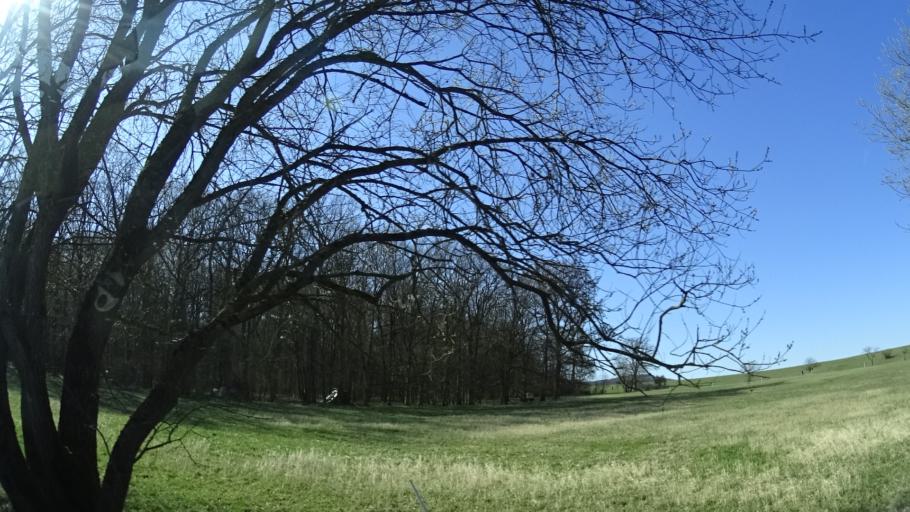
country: DE
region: Thuringia
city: Dingsleben
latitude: 50.4133
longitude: 10.6249
